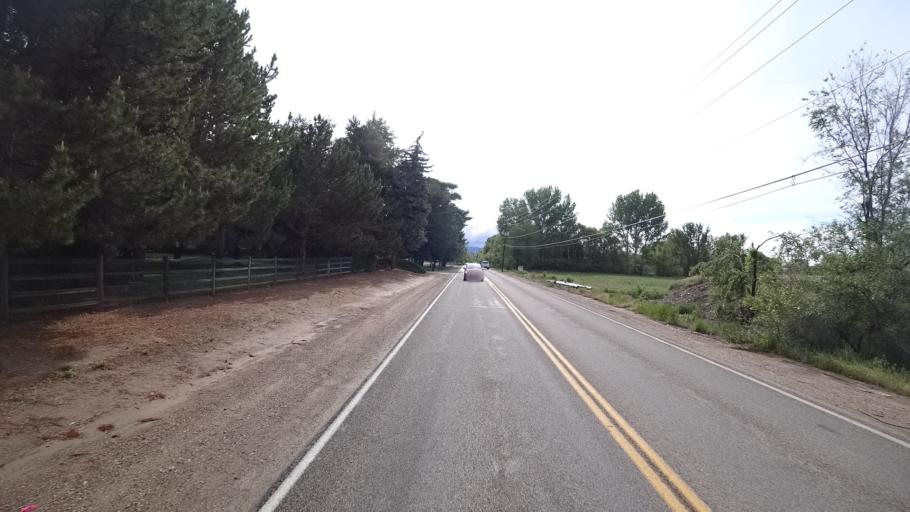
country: US
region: Idaho
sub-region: Ada County
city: Eagle
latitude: 43.7208
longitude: -116.3457
